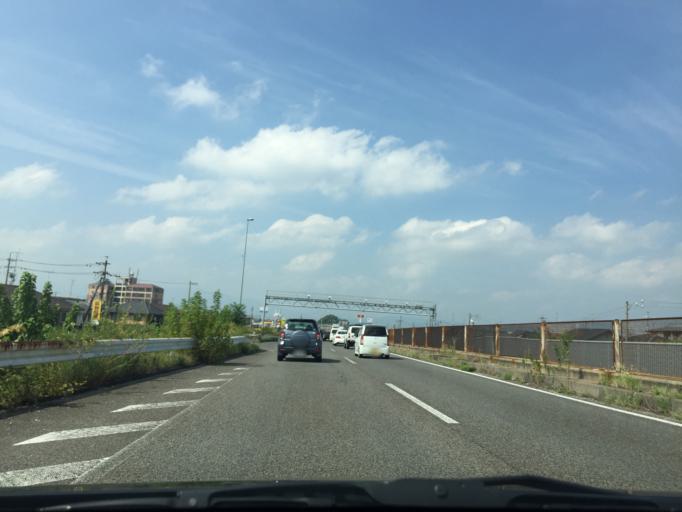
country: JP
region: Gifu
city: Ogaki
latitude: 35.3818
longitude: 136.6753
